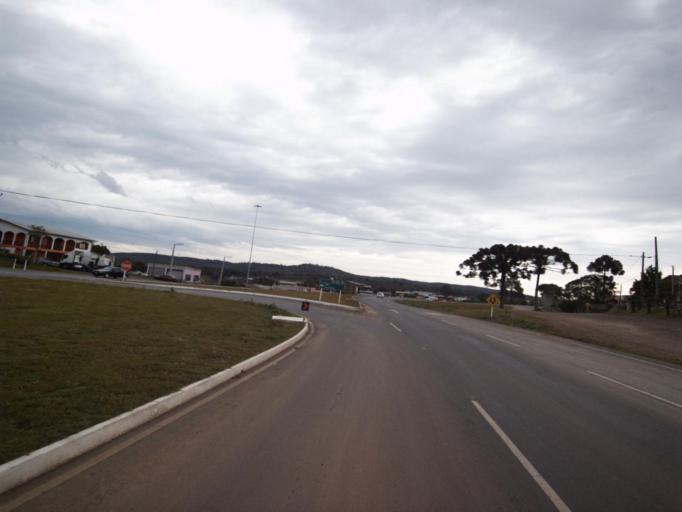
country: BR
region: Santa Catarina
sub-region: Concordia
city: Concordia
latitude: -27.0242
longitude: -51.8856
